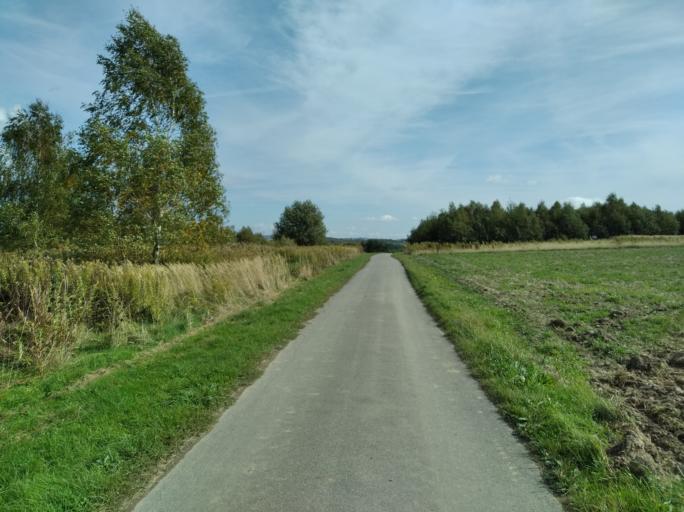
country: PL
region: Subcarpathian Voivodeship
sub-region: Powiat strzyzowski
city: Jawornik
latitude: 49.8399
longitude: 21.8755
